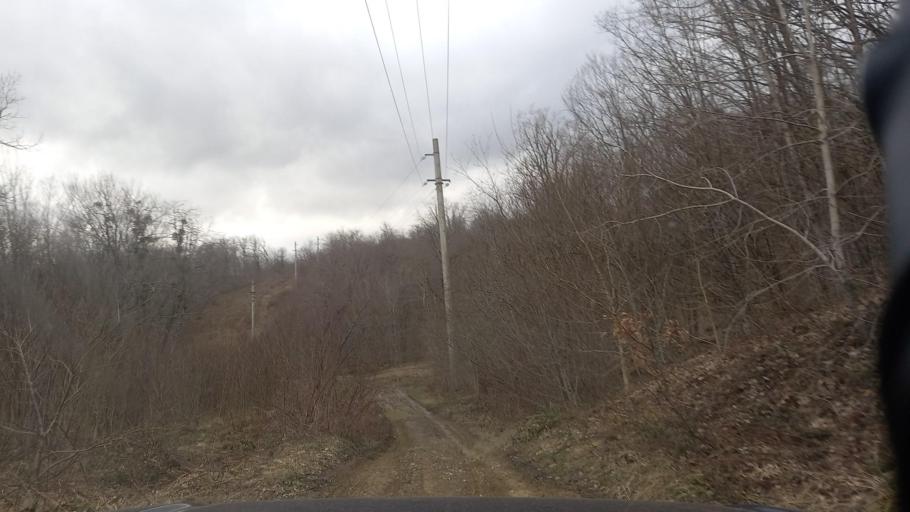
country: RU
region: Krasnodarskiy
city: Dzhubga
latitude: 44.4879
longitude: 38.7707
